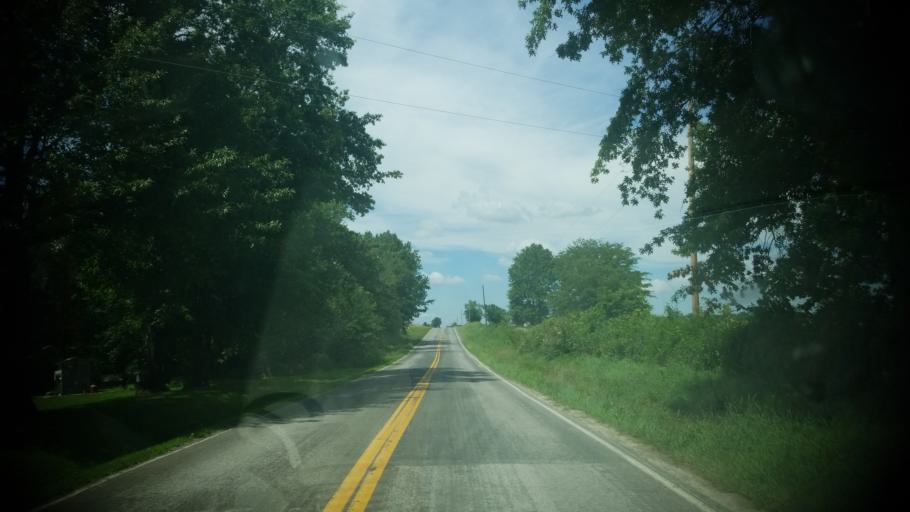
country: US
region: Missouri
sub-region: Audrain County
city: Vandalia
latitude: 39.3208
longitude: -91.3452
